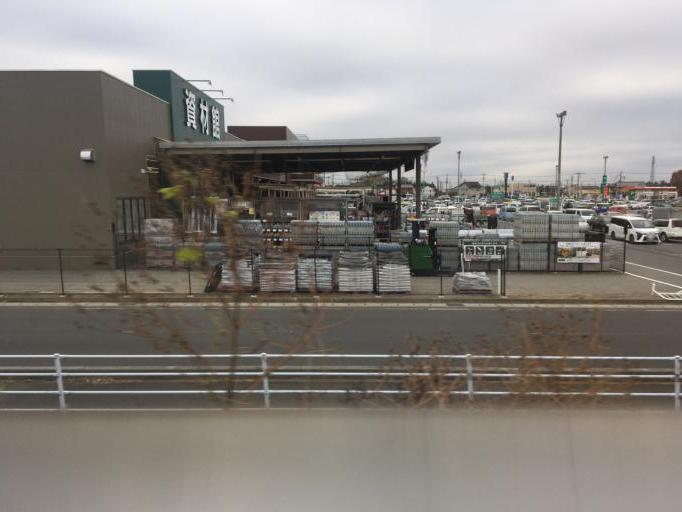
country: JP
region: Tochigi
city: Tochigi
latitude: 36.3543
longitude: 139.7086
